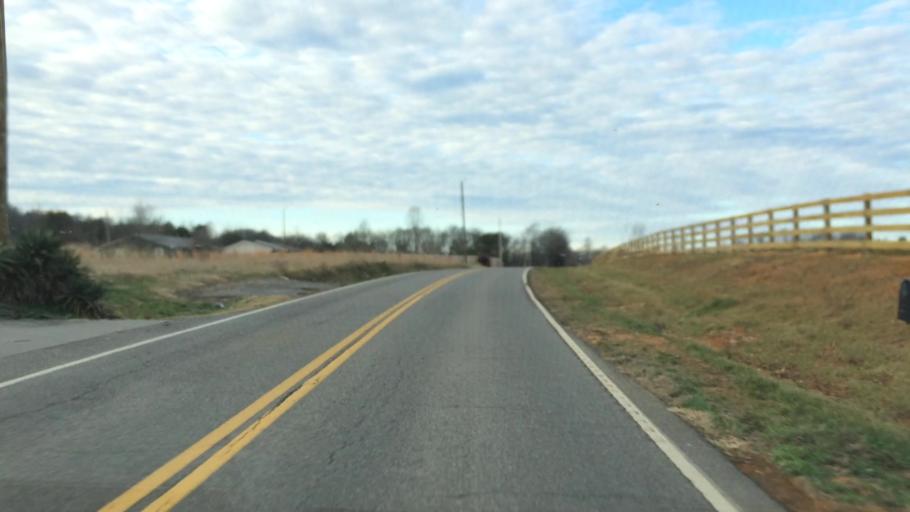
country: US
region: Tennessee
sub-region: McMinn County
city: Athens
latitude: 35.4745
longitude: -84.5336
